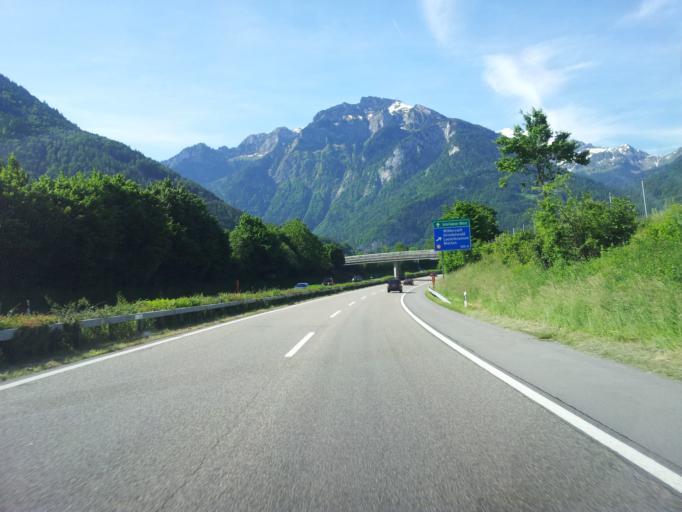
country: CH
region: Bern
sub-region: Interlaken-Oberhasli District
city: Matten
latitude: 46.6780
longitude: 7.8756
